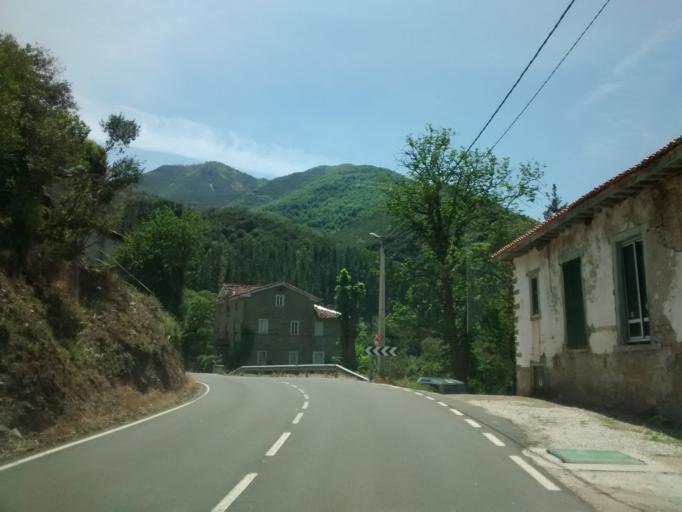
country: ES
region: Cantabria
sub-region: Provincia de Cantabria
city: Potes
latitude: 43.1217
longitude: -4.6293
